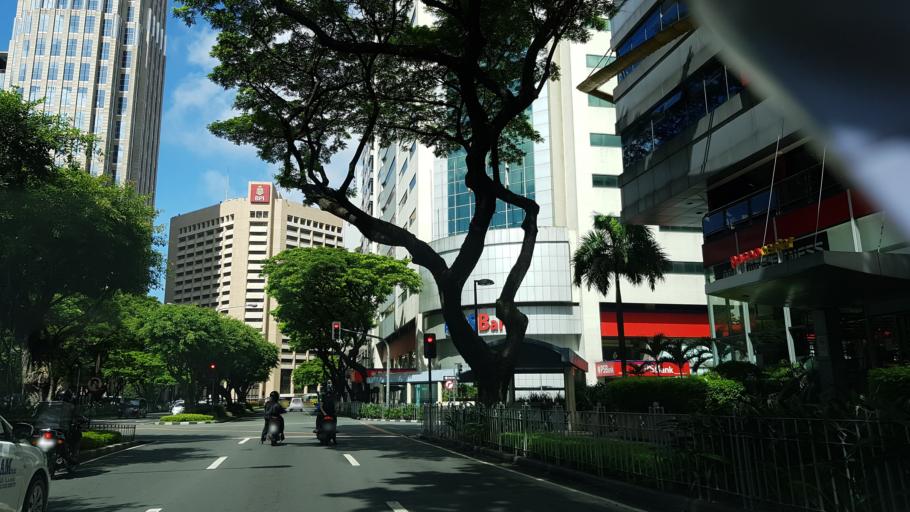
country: PH
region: Metro Manila
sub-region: Makati City
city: Makati City
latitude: 14.5576
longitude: 121.0231
